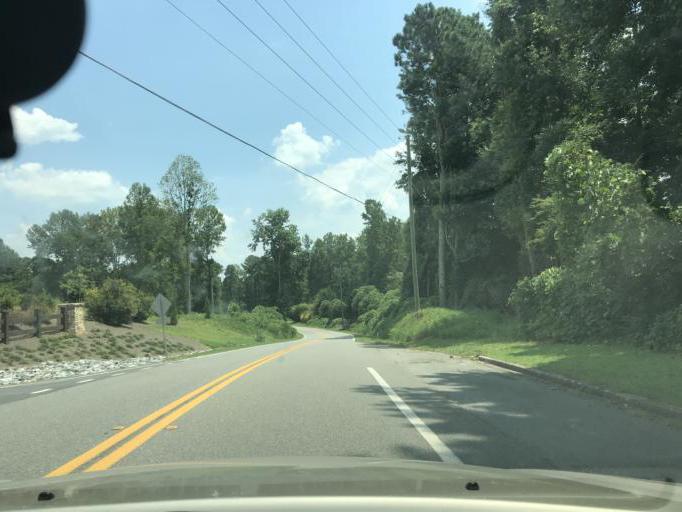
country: US
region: Georgia
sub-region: Forsyth County
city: Cumming
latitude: 34.2719
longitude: -84.1632
